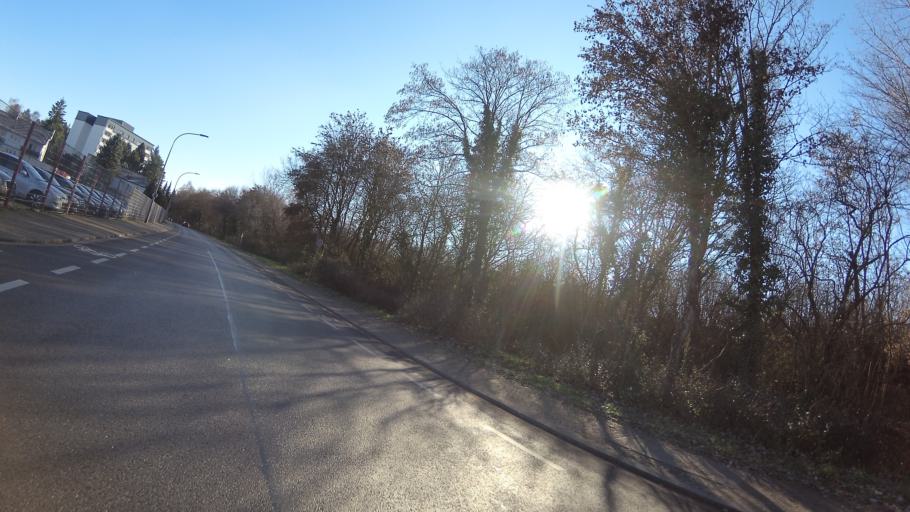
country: DE
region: Saarland
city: Saarlouis
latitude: 49.3092
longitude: 6.7328
